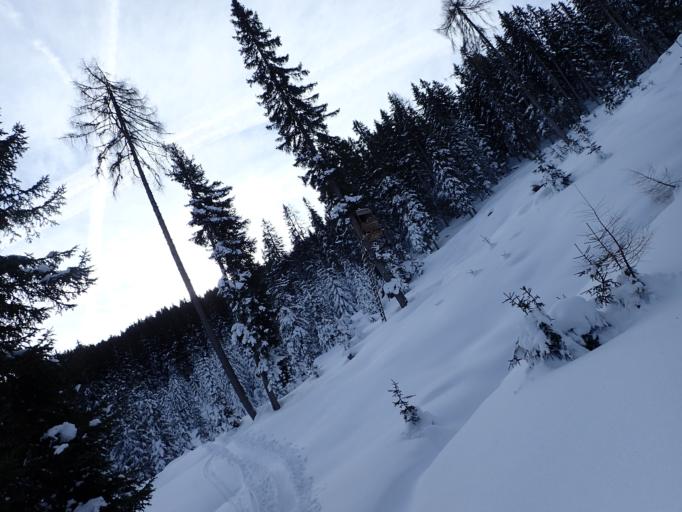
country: AT
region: Salzburg
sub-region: Politischer Bezirk Zell am See
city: Lend
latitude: 47.2738
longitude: 13.0137
